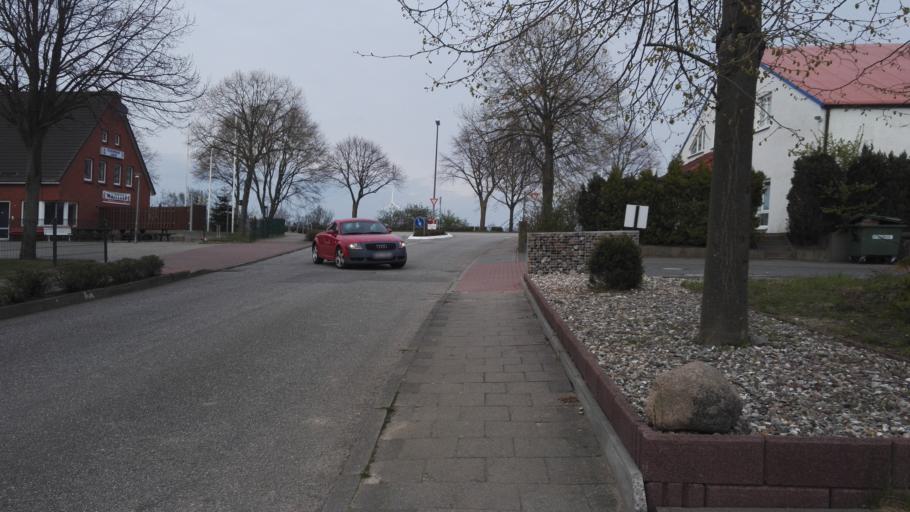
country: DE
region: Schleswig-Holstein
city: Laboe
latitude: 54.3983
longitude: 10.2322
